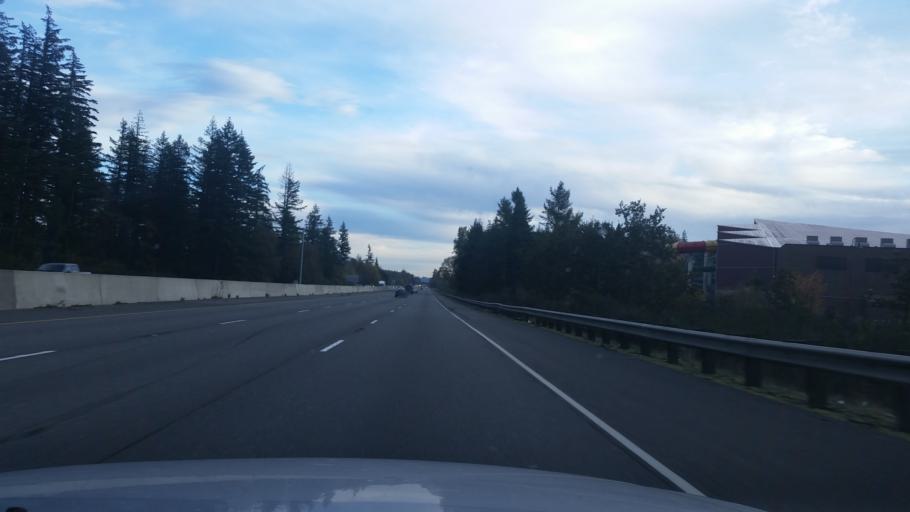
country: US
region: Washington
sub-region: Thurston County
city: Grand Mound
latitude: 46.7921
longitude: -123.0095
